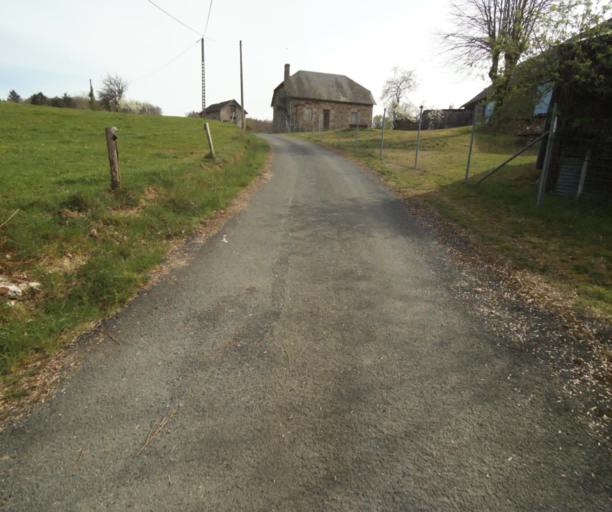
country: FR
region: Limousin
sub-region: Departement de la Correze
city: Correze
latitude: 45.3910
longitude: 1.8225
